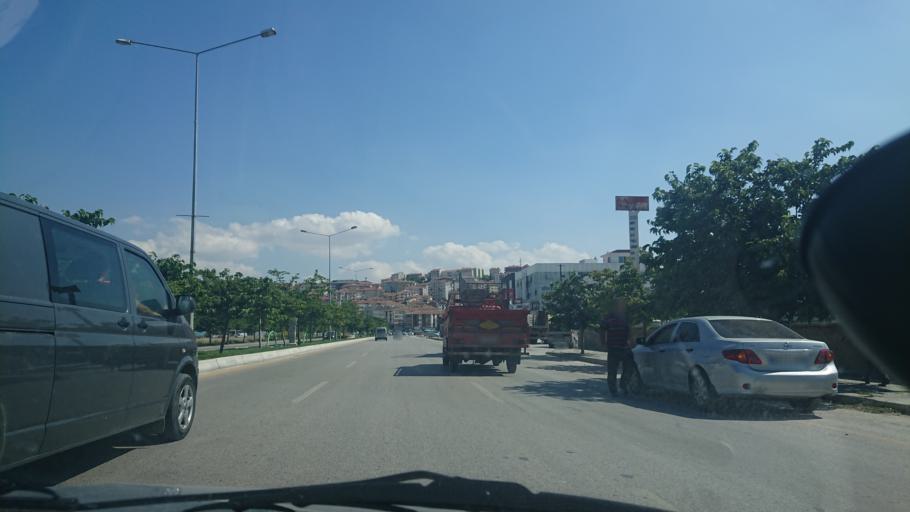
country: TR
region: Ankara
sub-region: Goelbasi
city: Golbasi
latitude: 39.8024
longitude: 32.8095
